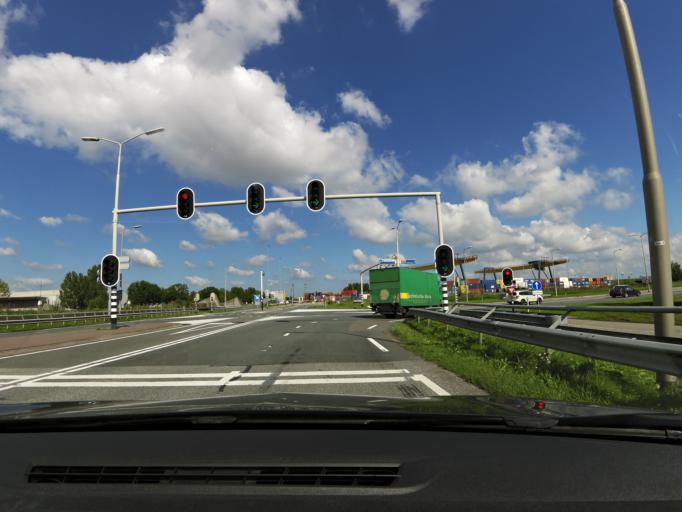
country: NL
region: South Holland
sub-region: Gemeente Alphen aan den Rijn
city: Alphen aan den Rijn
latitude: 52.1105
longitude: 4.6708
